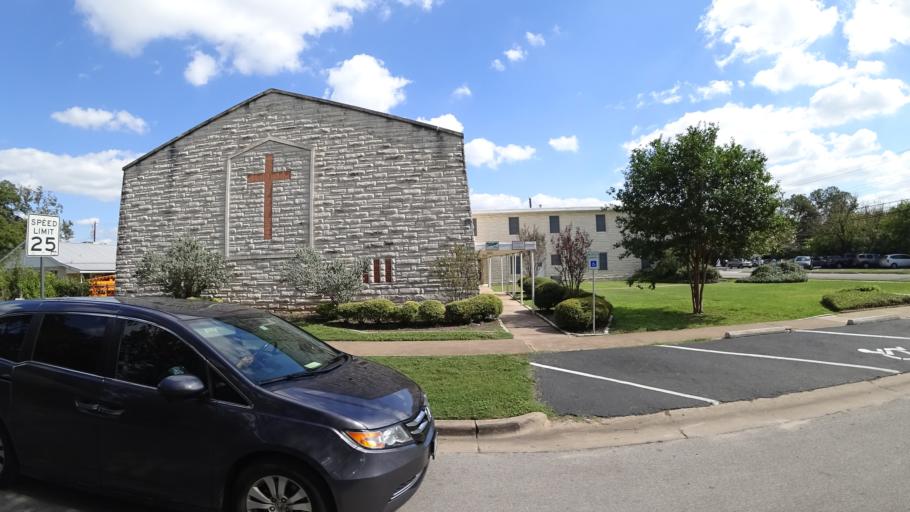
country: US
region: Texas
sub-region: Travis County
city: Austin
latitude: 30.3132
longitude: -97.7169
